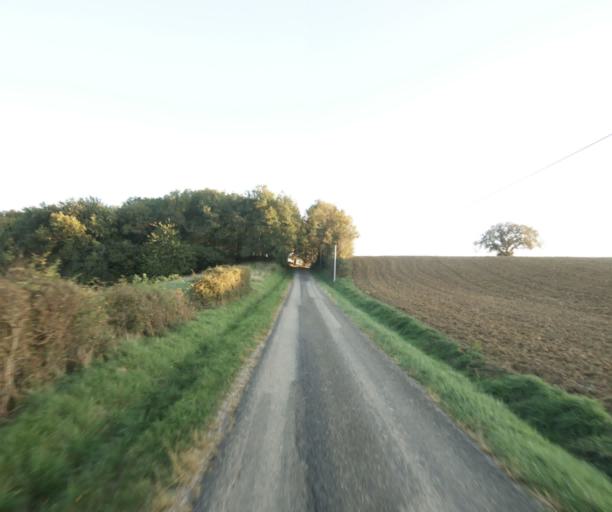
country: FR
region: Midi-Pyrenees
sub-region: Departement du Gers
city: Vic-Fezensac
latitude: 43.7552
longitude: 0.1970
